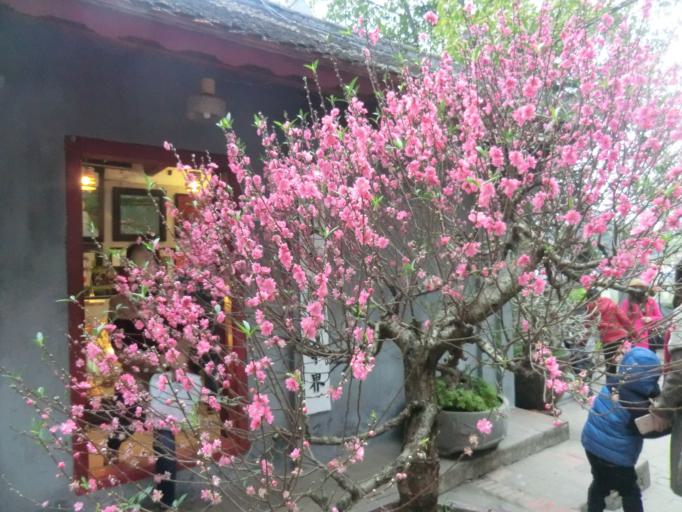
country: VN
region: Ha Noi
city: Hoan Kiem
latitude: 21.0306
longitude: 105.8523
